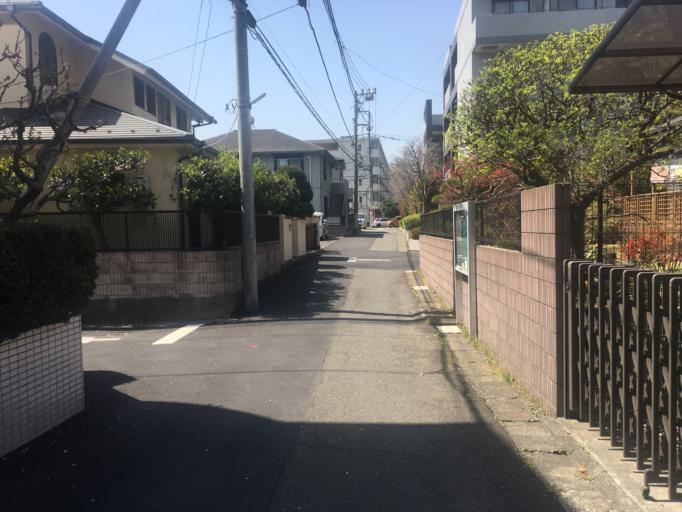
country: JP
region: Tokyo
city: Kokubunji
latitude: 35.7025
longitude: 139.4782
